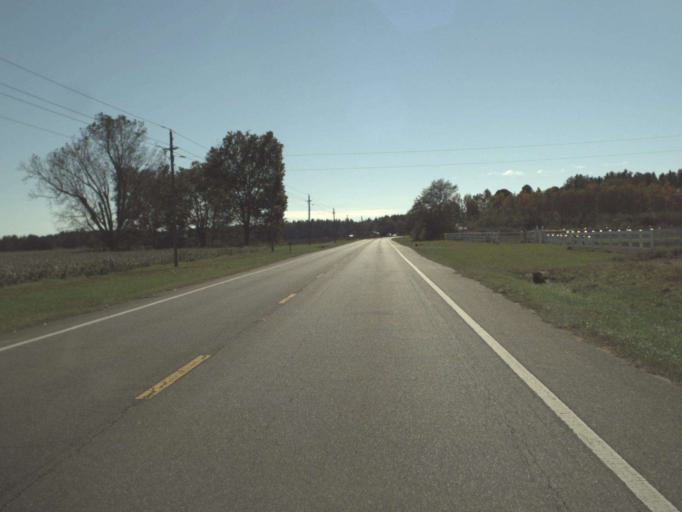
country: US
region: Florida
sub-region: Okaloosa County
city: Crestview
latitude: 30.8313
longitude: -86.6754
